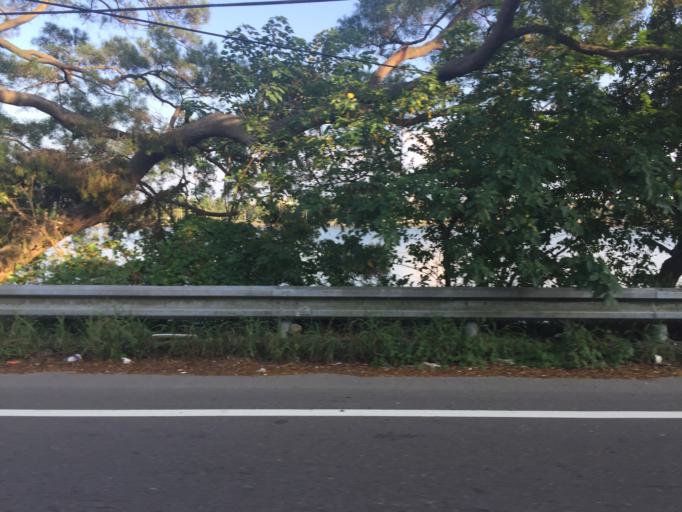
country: TW
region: Taiwan
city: Daxi
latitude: 24.9146
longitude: 121.2548
